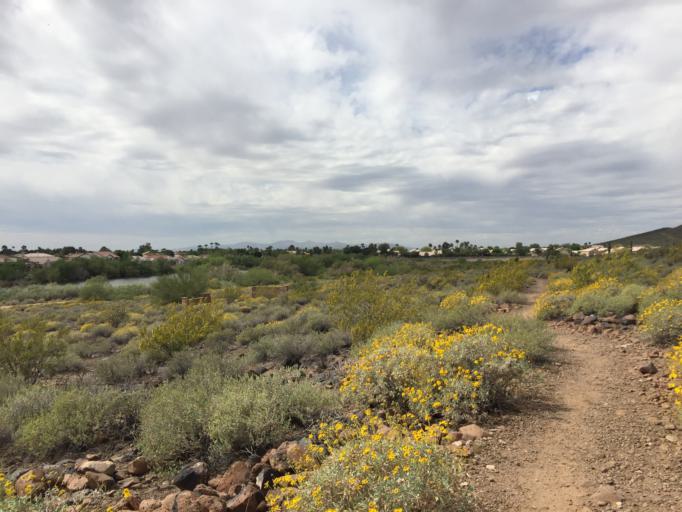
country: US
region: Arizona
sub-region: Maricopa County
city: Peoria
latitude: 33.6851
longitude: -112.1813
